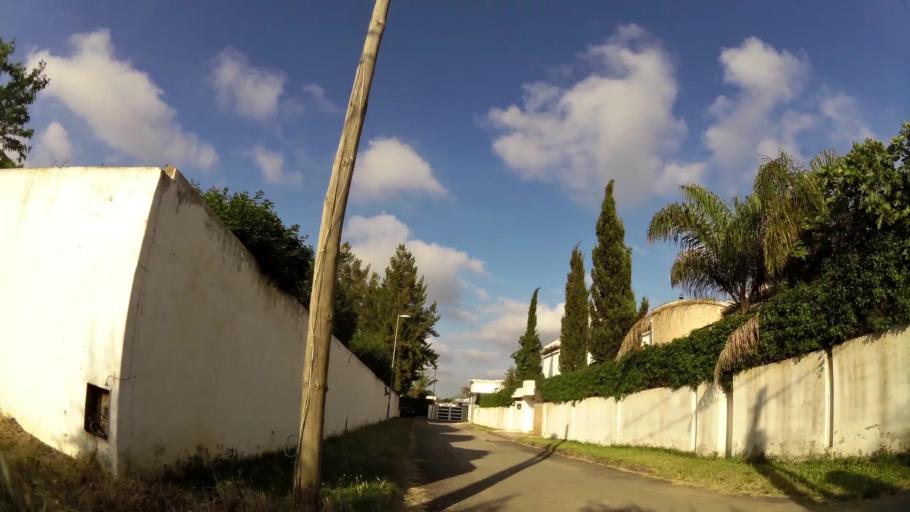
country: MA
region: Rabat-Sale-Zemmour-Zaer
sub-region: Rabat
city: Rabat
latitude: 33.9563
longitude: -6.8454
